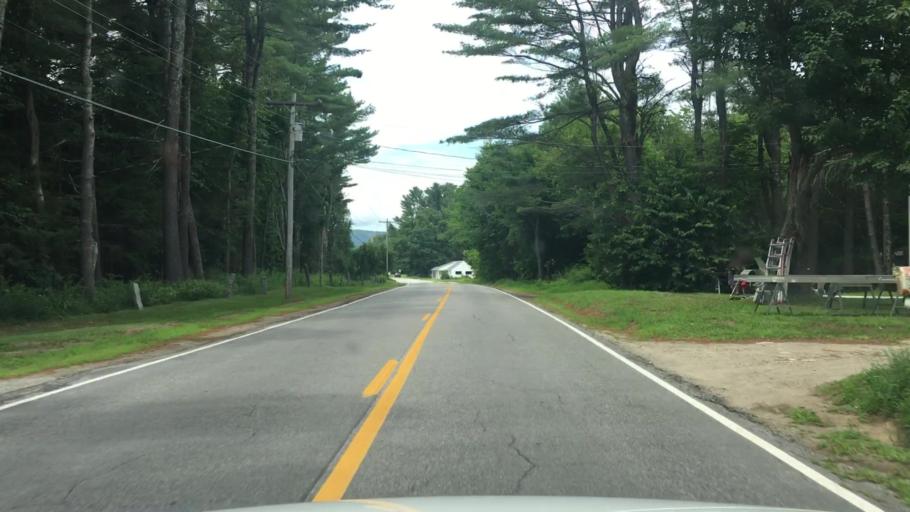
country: US
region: New Hampshire
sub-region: Grafton County
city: Rumney
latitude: 43.7822
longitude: -71.7634
